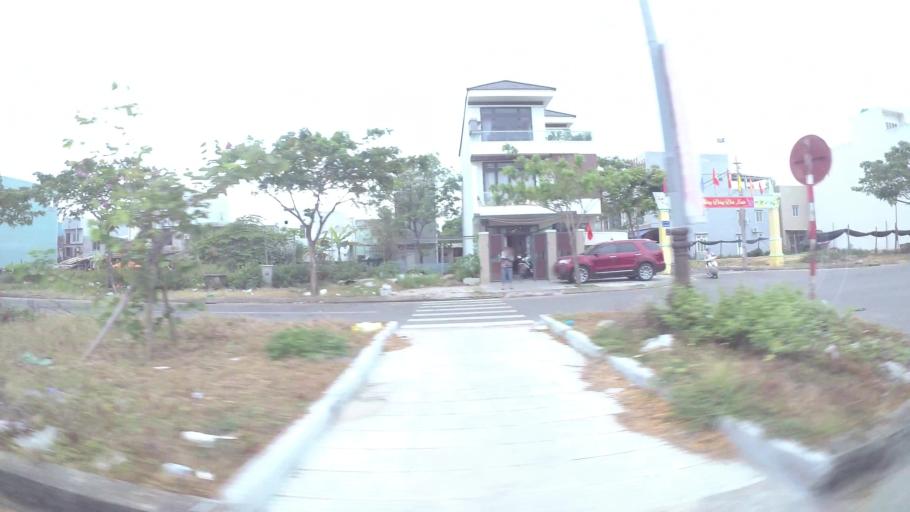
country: VN
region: Da Nang
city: Da Nang
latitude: 16.0926
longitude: 108.2348
